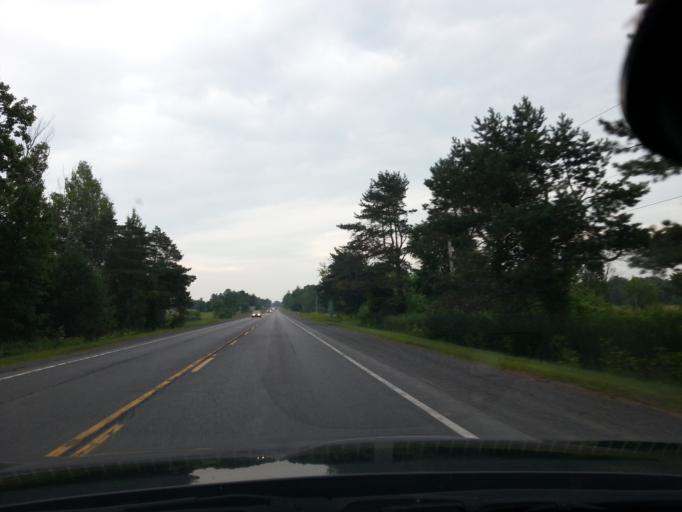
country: CA
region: Quebec
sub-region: Outaouais
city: Thurso
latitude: 45.5711
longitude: -75.1593
